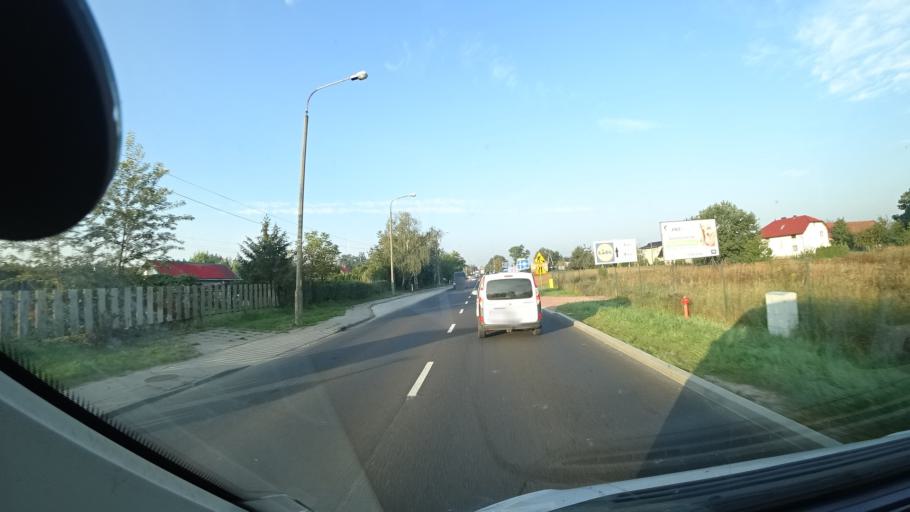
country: PL
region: Opole Voivodeship
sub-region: Powiat kedzierzynsko-kozielski
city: Kedzierzyn-Kozle
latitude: 50.3550
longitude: 18.2460
